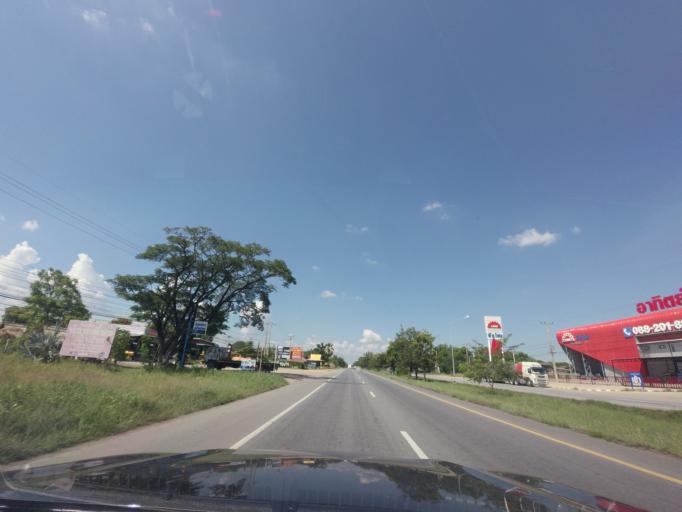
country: TH
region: Nakhon Ratchasima
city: Non Sung
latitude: 15.1531
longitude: 102.3273
